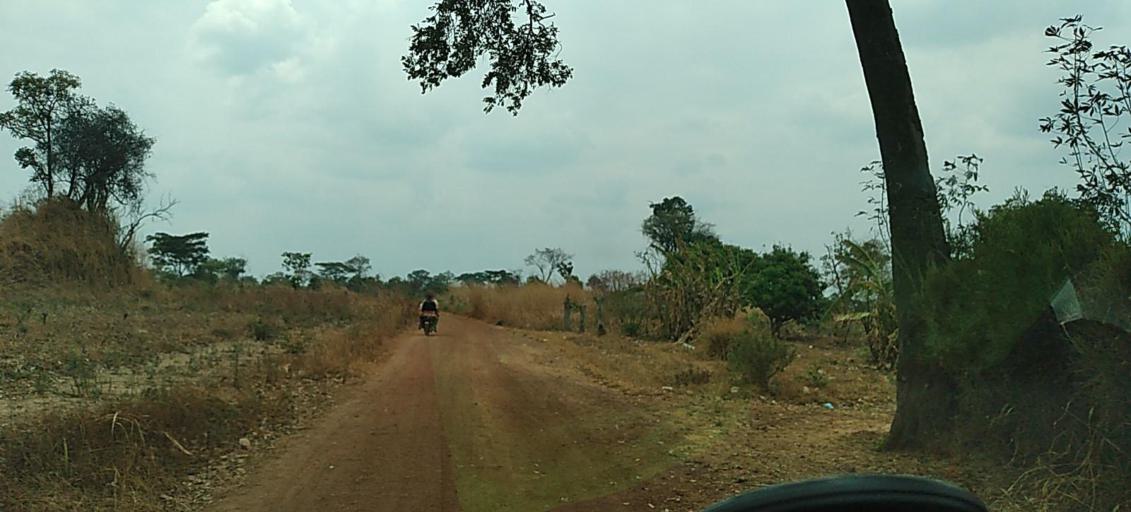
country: ZM
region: North-Western
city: Kansanshi
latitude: -12.0885
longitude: 26.3659
